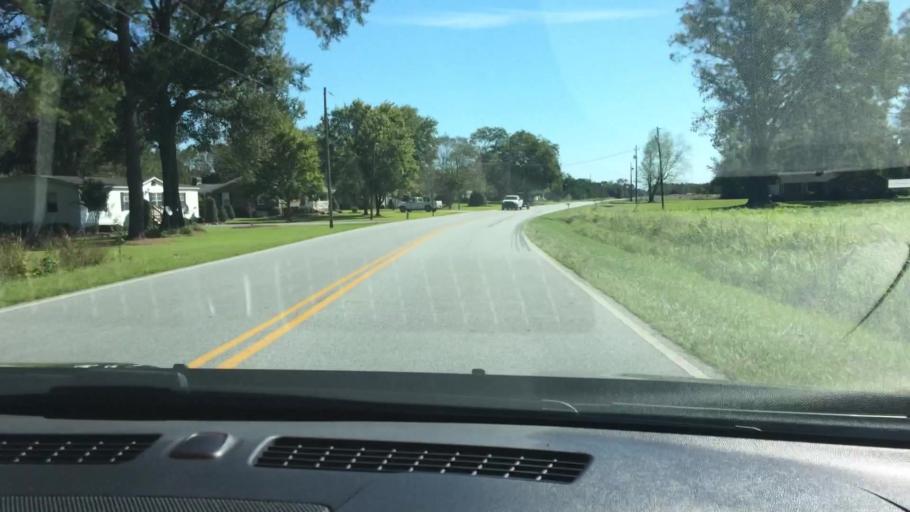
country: US
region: North Carolina
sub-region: Pitt County
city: Grifton
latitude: 35.3963
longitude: -77.3976
